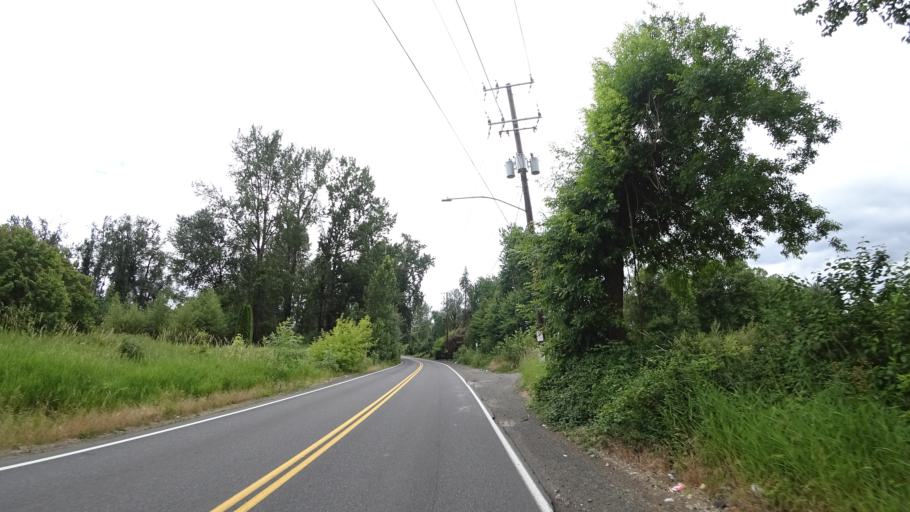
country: US
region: Oregon
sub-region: Multnomah County
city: Lents
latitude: 45.5718
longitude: -122.5858
